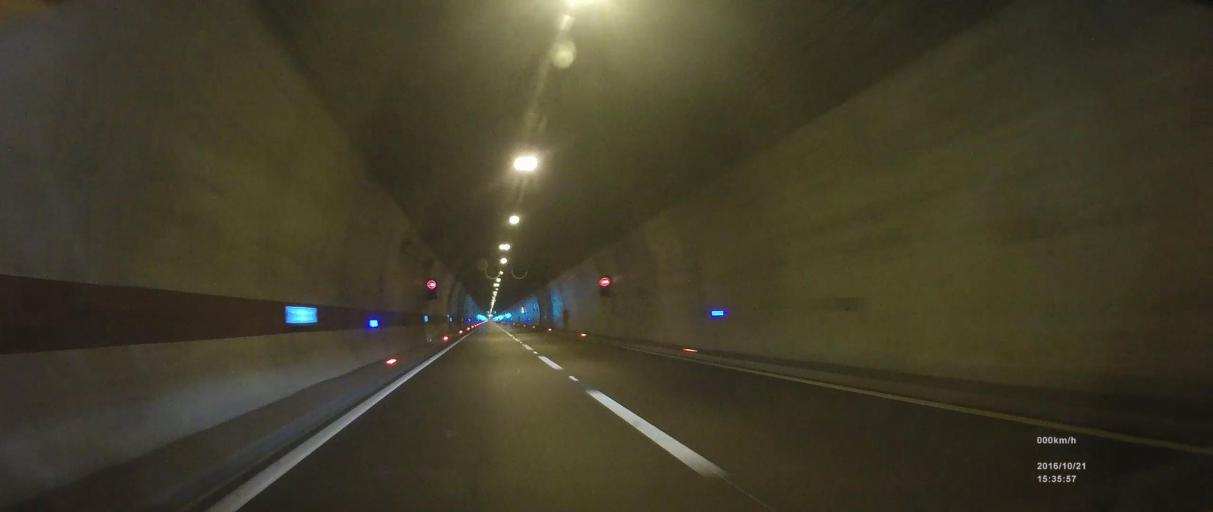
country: HR
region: Zadarska
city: Obrovac
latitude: 44.2648
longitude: 15.6556
